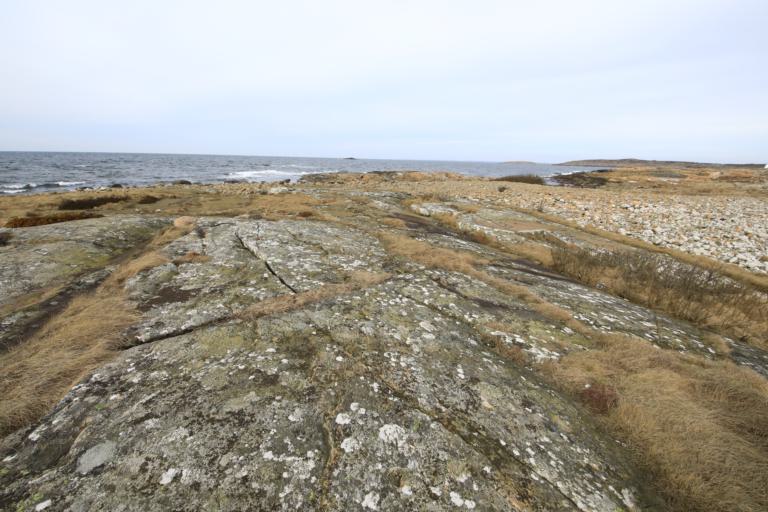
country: SE
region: Halland
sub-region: Kungsbacka Kommun
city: Frillesas
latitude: 57.2360
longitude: 12.0954
